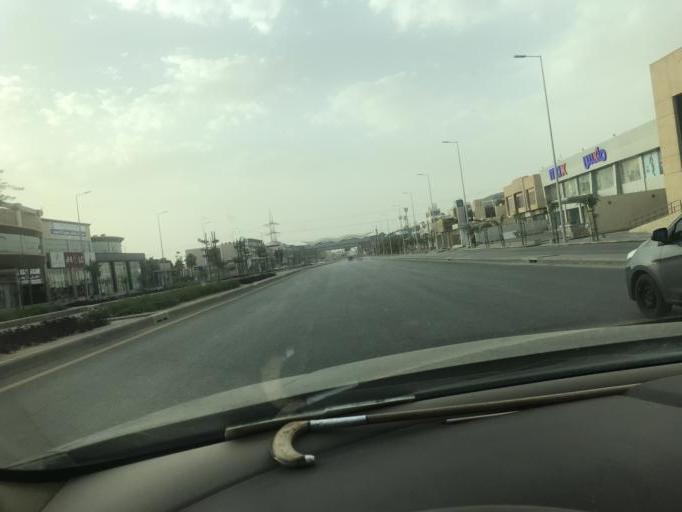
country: SA
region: Ar Riyad
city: Riyadh
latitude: 24.7808
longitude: 46.6631
